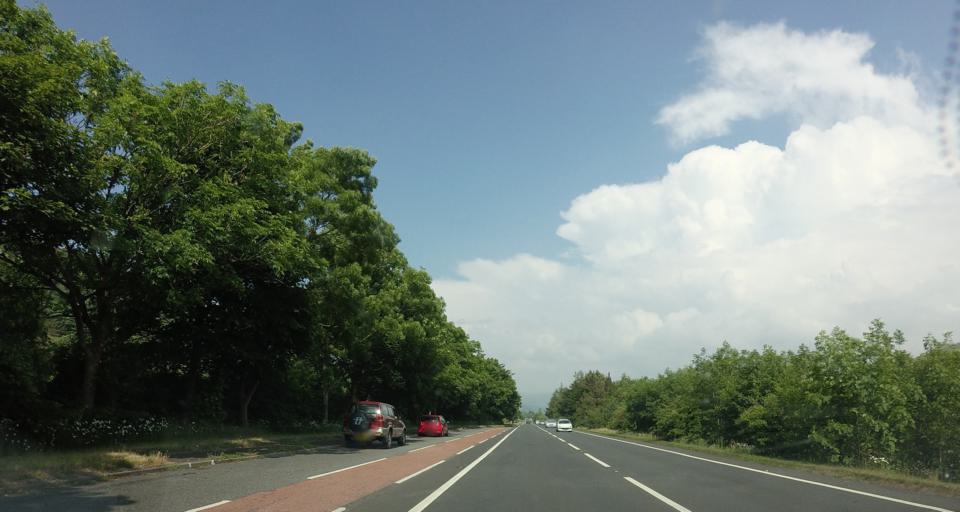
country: GB
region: England
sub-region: Cumbria
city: Cockermouth
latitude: 54.6632
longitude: -3.2735
